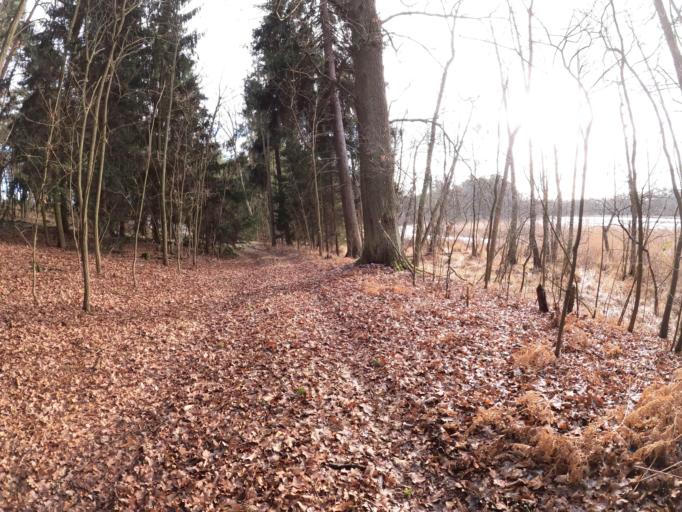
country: PL
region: Lubusz
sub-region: Powiat slubicki
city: Cybinka
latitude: 52.2599
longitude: 14.7939
